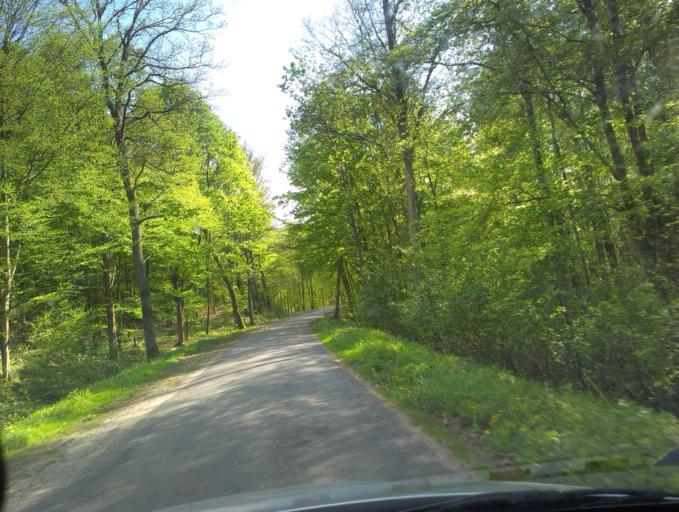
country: PL
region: West Pomeranian Voivodeship
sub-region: Powiat szczecinecki
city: Barwice
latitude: 53.7077
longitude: 16.2997
